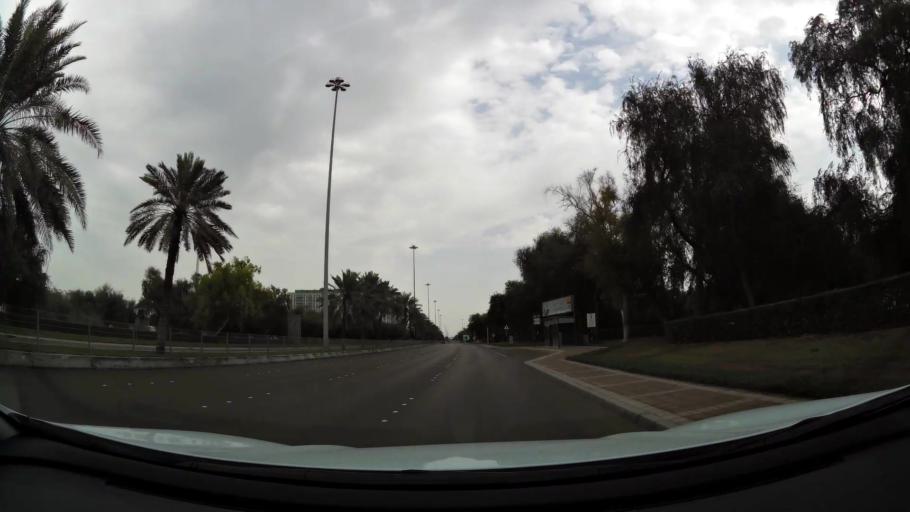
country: AE
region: Abu Dhabi
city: Abu Dhabi
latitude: 24.4294
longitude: 54.4226
